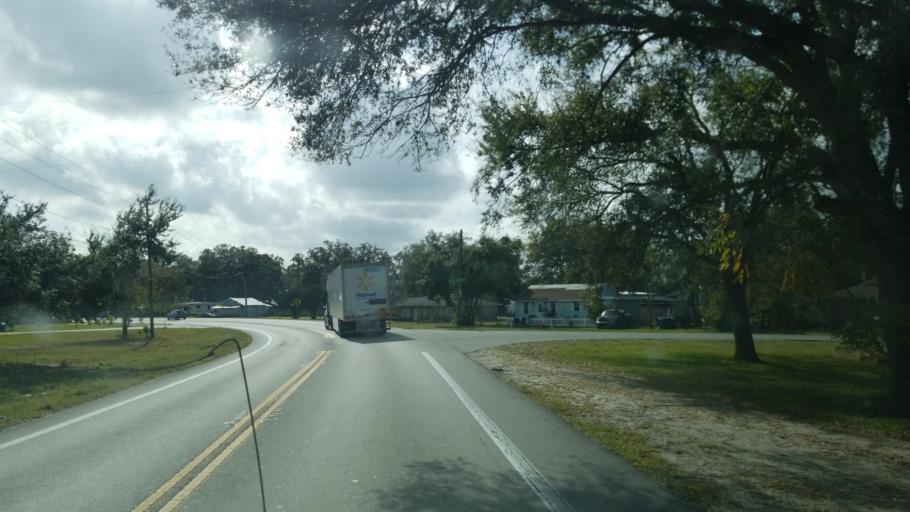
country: US
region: Florida
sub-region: Polk County
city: Haines City
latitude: 28.1224
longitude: -81.6487
